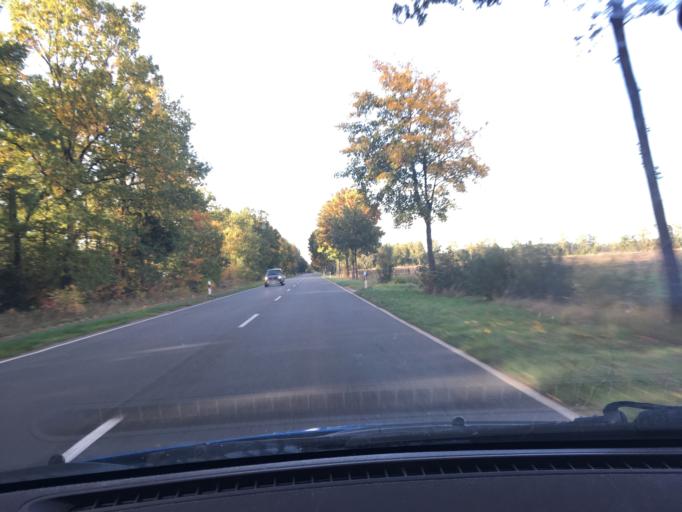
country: DE
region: Lower Saxony
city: Fassberg
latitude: 52.9431
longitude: 10.1315
